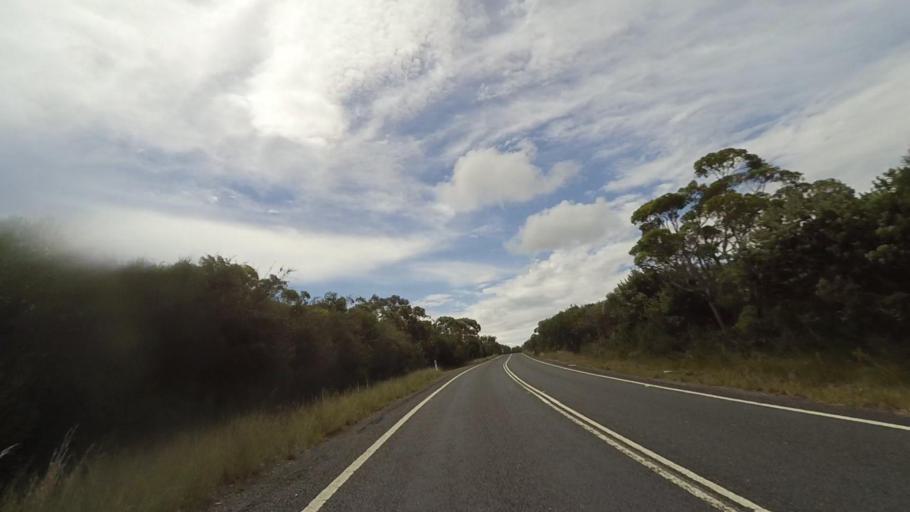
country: AU
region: New South Wales
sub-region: Sutherland Shire
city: Heathcote
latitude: -34.1121
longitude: 151.0599
